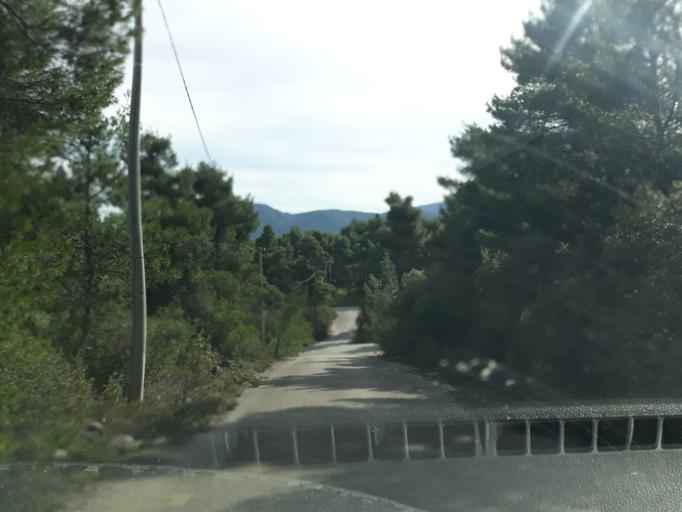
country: GR
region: Attica
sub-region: Nomarchia Anatolikis Attikis
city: Afidnes
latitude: 38.2156
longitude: 23.7946
